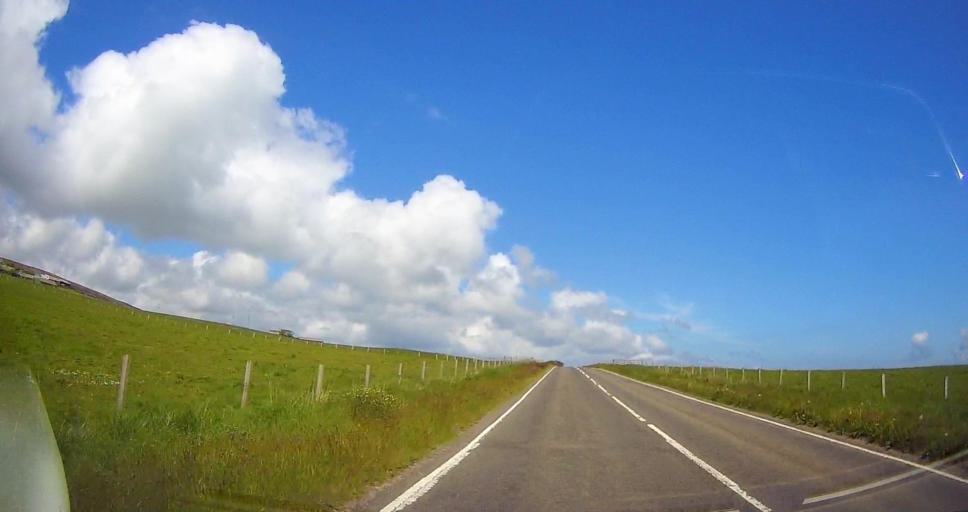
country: GB
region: Scotland
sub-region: Orkney Islands
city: Orkney
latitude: 59.0182
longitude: -3.1032
